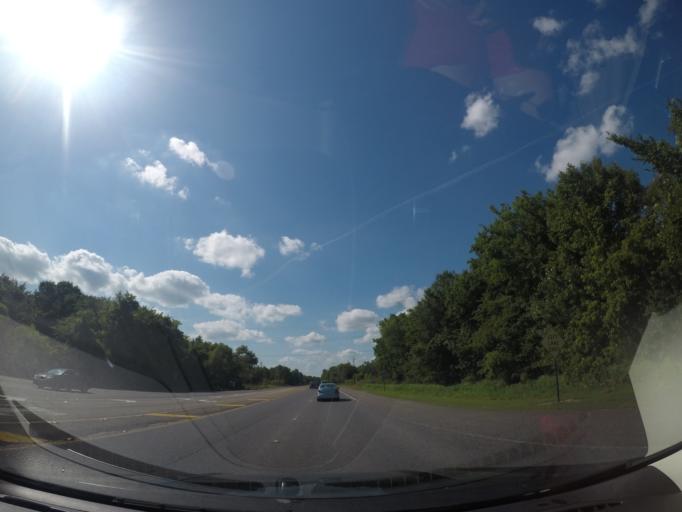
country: US
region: Louisiana
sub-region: Saint James Parish
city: Gramercy
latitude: 30.0743
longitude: -90.6836
